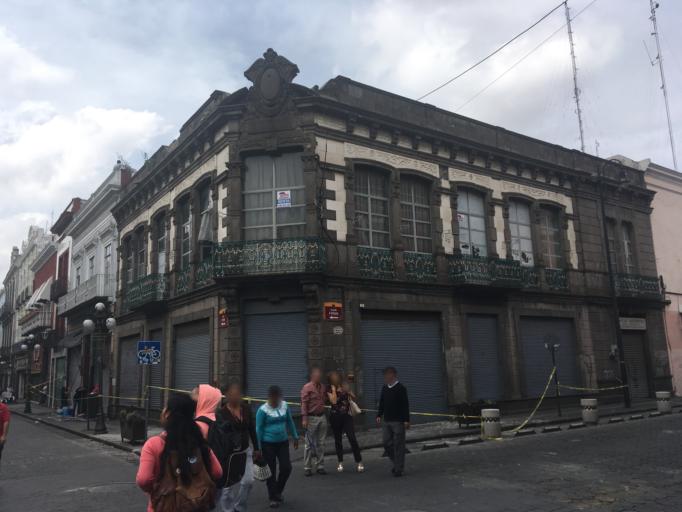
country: MX
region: Puebla
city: Puebla
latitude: 19.0453
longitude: -98.1963
